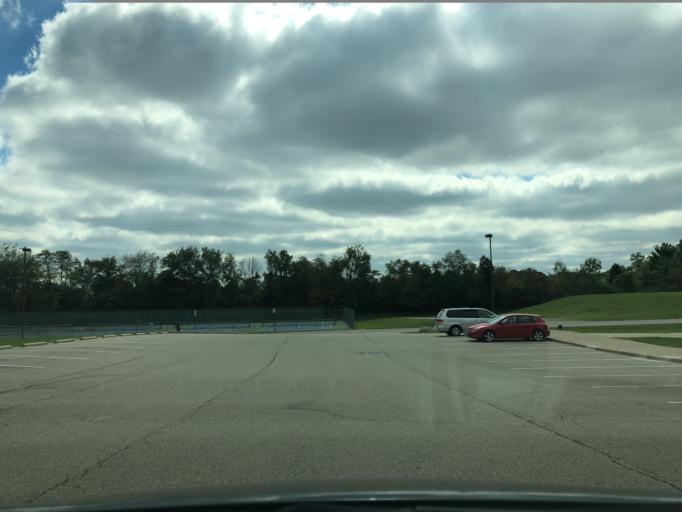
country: US
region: Ohio
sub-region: Hamilton County
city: Loveland
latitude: 39.2793
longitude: -84.2740
